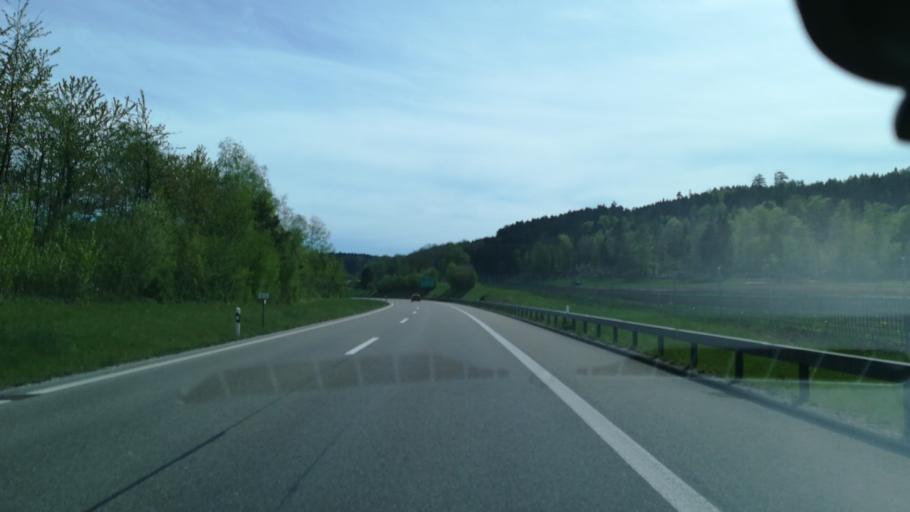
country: CH
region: Zurich
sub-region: Bezirk Winterthur
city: Sulz
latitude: 47.5317
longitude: 8.7922
